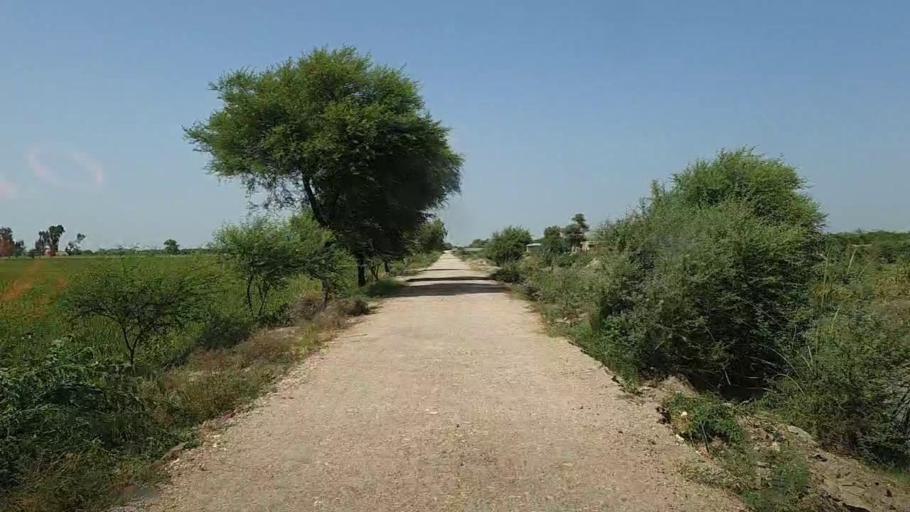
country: PK
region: Sindh
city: Kario
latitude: 24.6587
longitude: 68.5497
